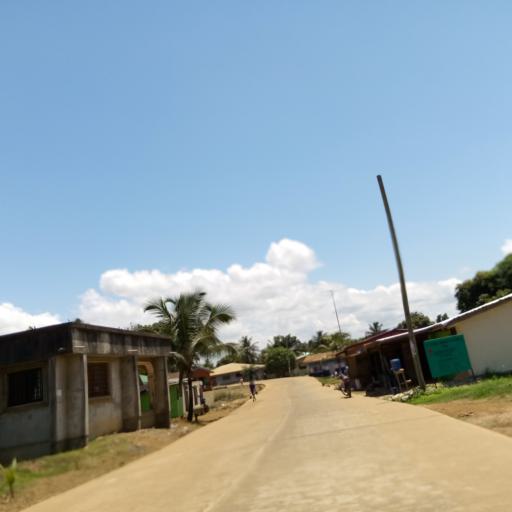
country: LR
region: Montserrado
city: Monrovia
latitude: 6.2474
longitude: -10.6912
